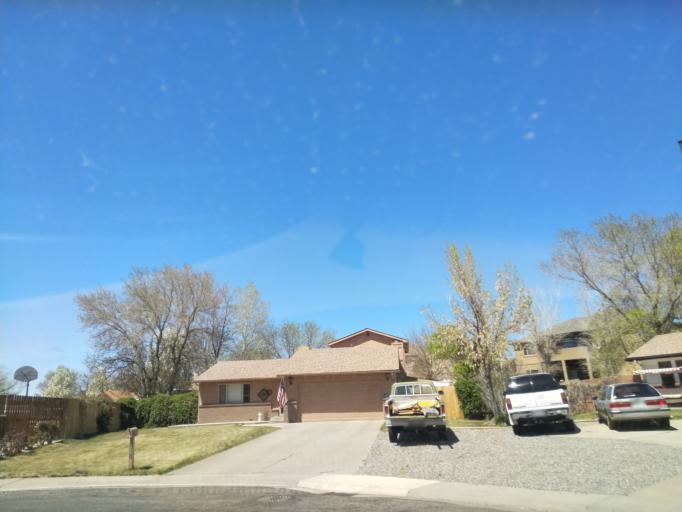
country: US
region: Colorado
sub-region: Mesa County
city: Grand Junction
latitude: 39.0961
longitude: -108.5420
